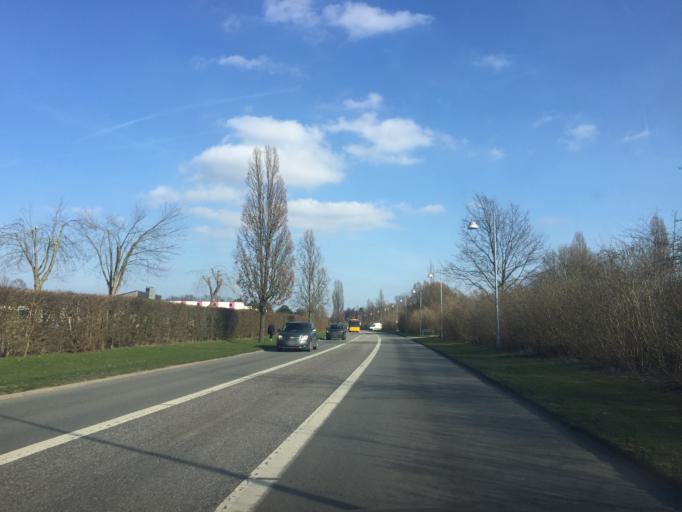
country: DK
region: Capital Region
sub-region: Albertslund Kommune
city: Albertslund
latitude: 55.6755
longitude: 12.3571
